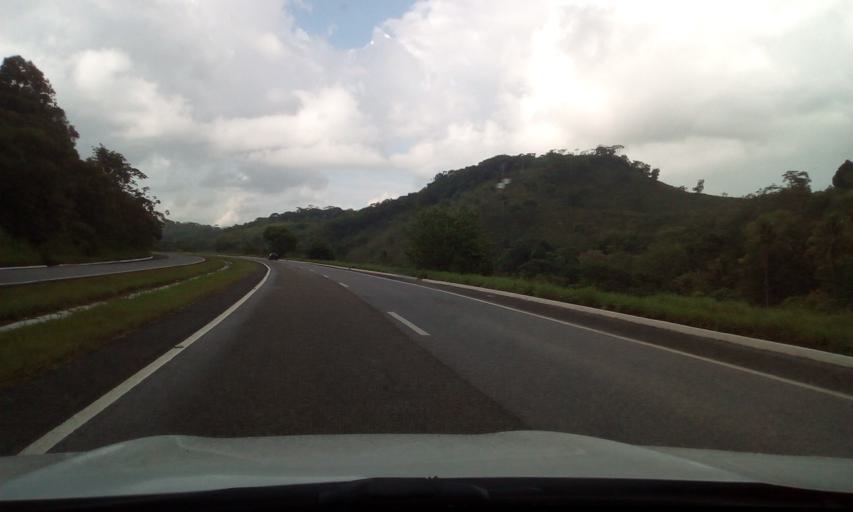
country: BR
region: Pernambuco
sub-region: Cabo De Santo Agostinho
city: Cabo
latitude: -8.2668
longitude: -35.0524
